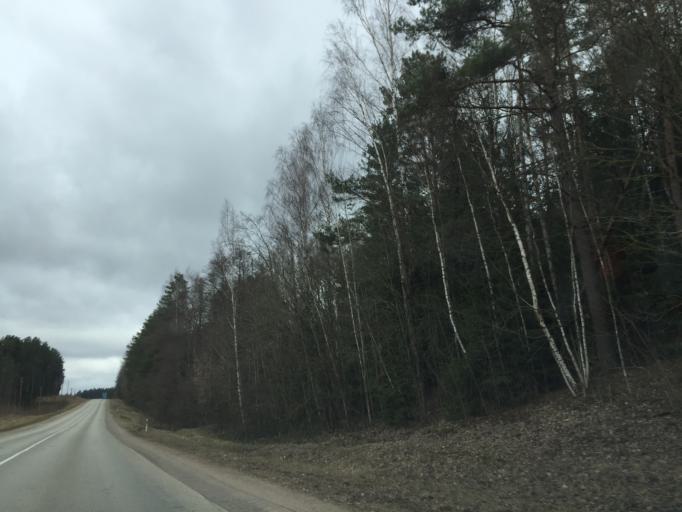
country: LV
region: Ilukste
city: Ilukste
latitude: 55.9187
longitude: 26.3271
